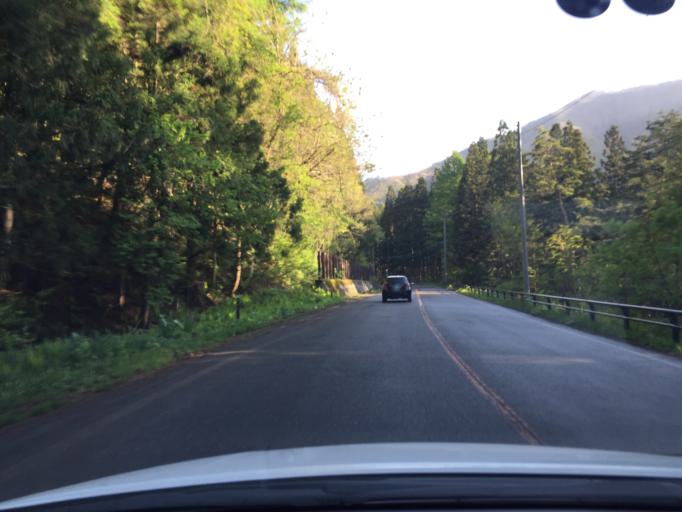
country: JP
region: Fukushima
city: Inawashiro
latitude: 37.6210
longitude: 140.1135
